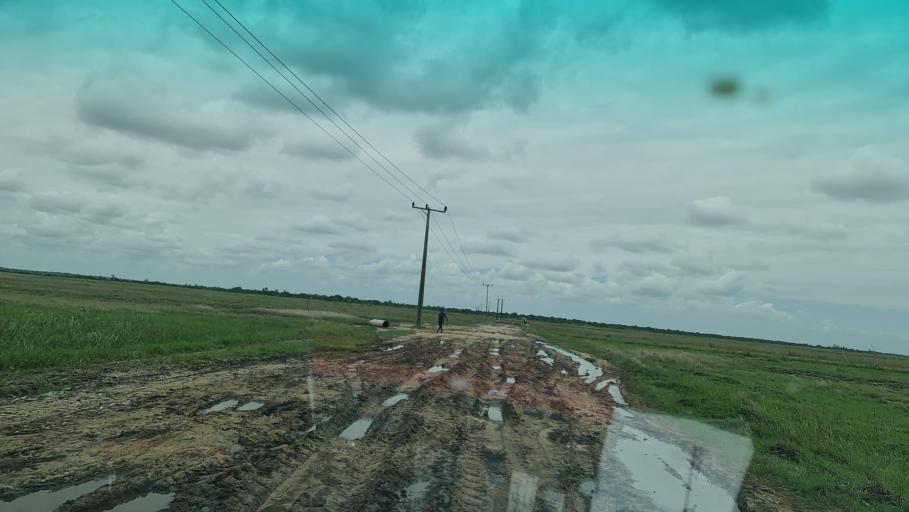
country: MZ
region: Maputo City
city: Maputo
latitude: -25.7132
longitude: 32.7027
